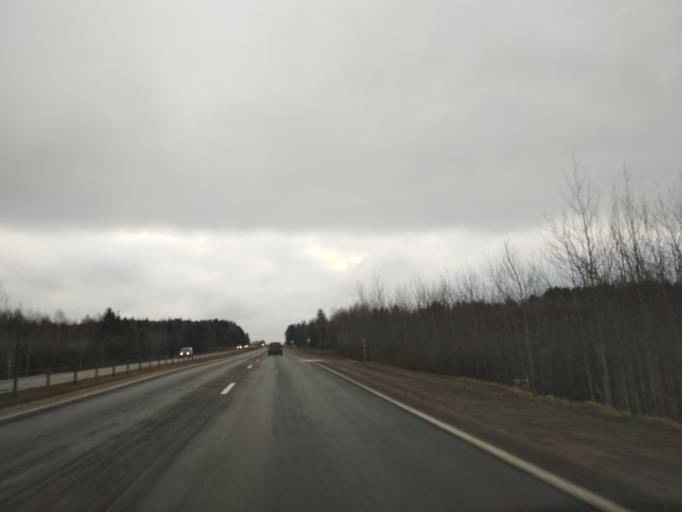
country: BY
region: Minsk
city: Luhavaya Slabada
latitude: 53.7186
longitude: 27.8648
